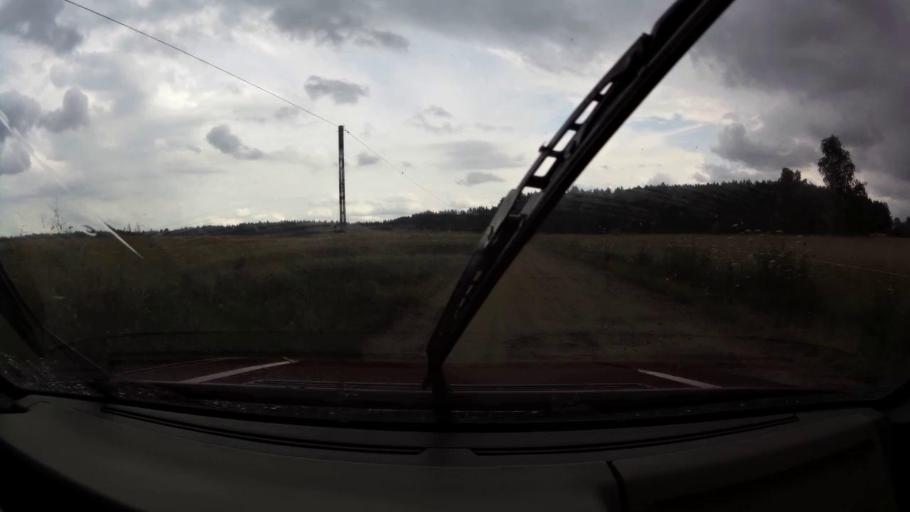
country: PL
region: West Pomeranian Voivodeship
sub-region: Powiat bialogardzki
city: Bialogard
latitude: 54.0690
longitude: 16.0979
